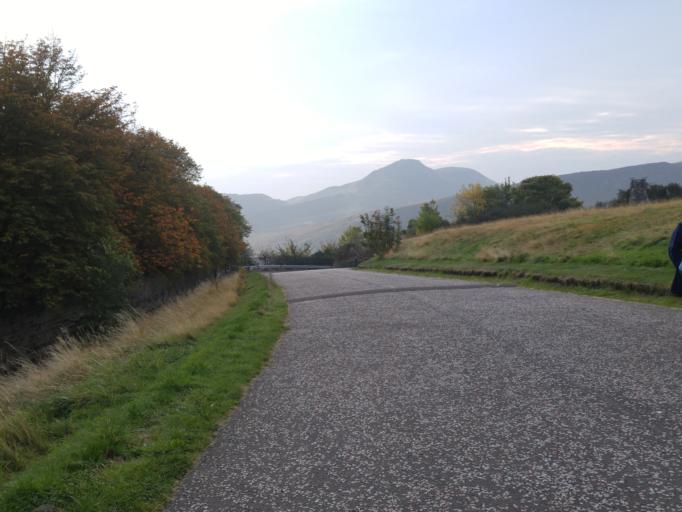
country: GB
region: Scotland
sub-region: Edinburgh
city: Edinburgh
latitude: 55.9549
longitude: -3.1800
